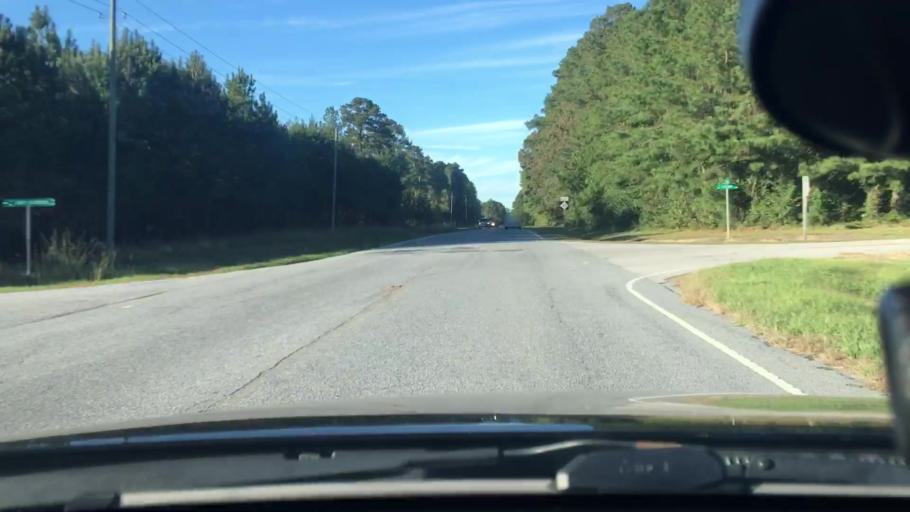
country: US
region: North Carolina
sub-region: Pitt County
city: Windsor
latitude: 35.4388
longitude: -77.2632
